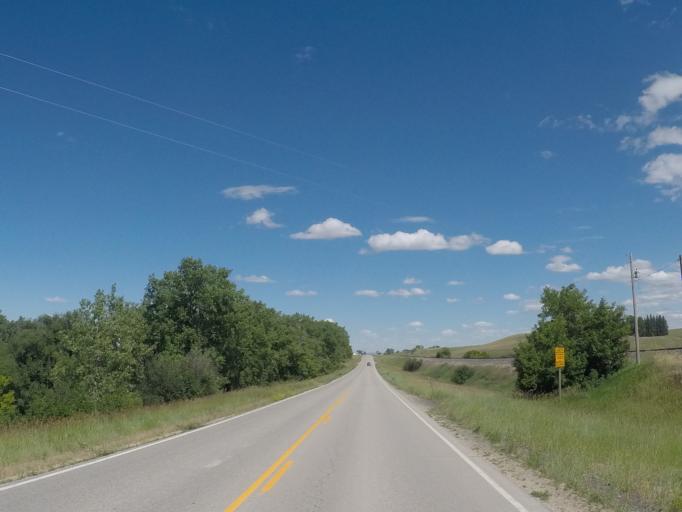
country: US
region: Wyoming
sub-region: Sheridan County
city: Sheridan
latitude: 44.9401
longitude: -107.2971
